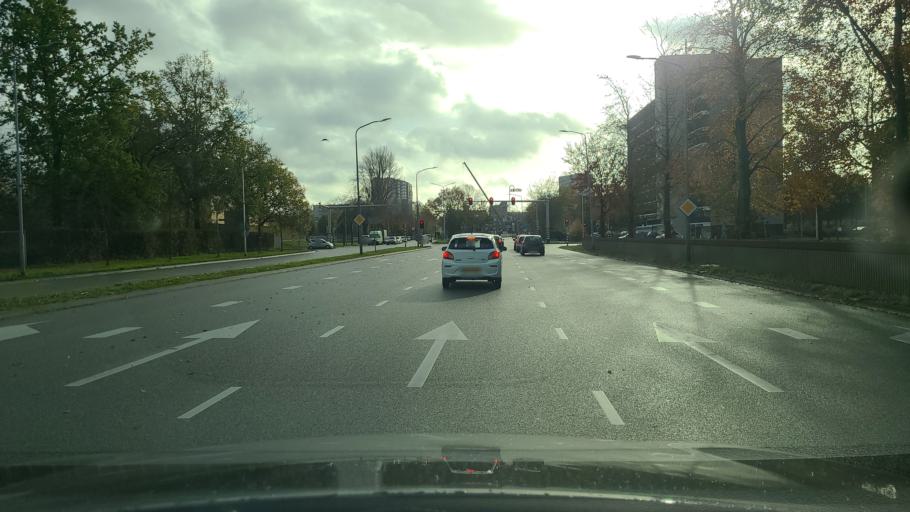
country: NL
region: Gelderland
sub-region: Gemeente Nijmegen
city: Lindenholt
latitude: 51.8328
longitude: 5.8186
